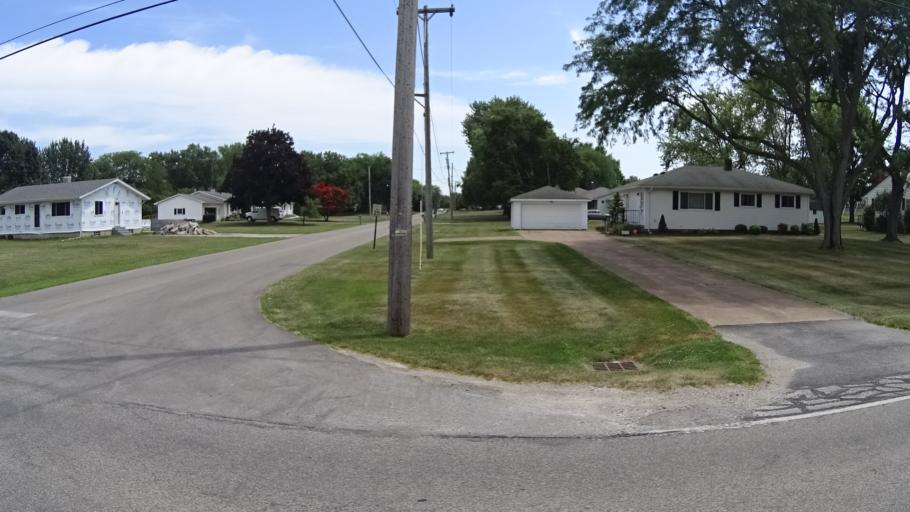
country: US
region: Ohio
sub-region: Erie County
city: Sandusky
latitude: 41.3983
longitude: -82.7847
